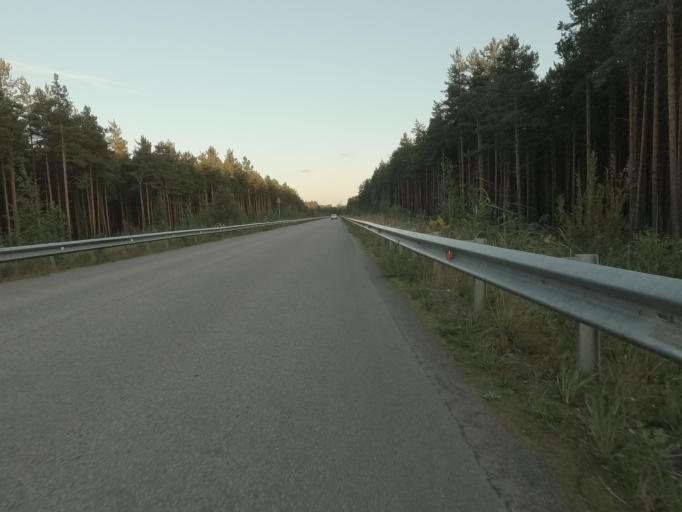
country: RU
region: Leningrad
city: Mga
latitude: 59.7662
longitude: 31.0338
